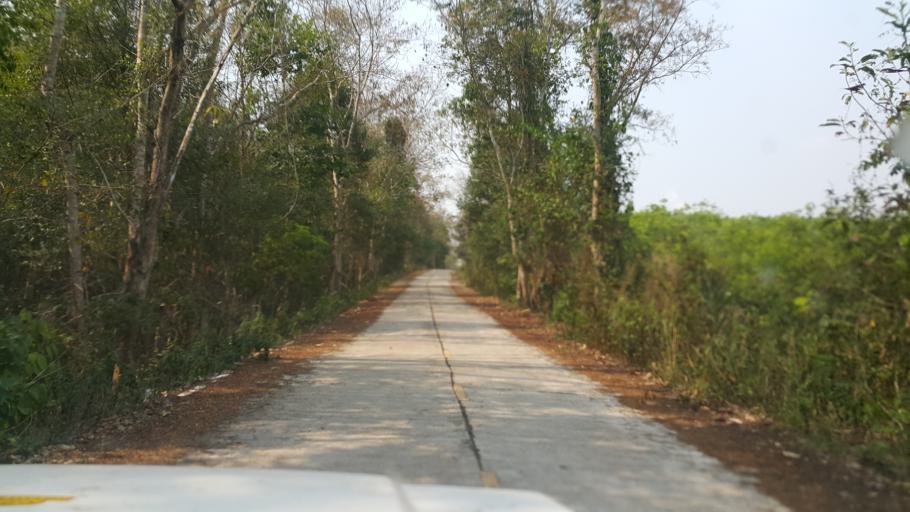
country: TH
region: Nakhon Phanom
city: Ban Phaeng
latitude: 17.9785
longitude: 104.1486
